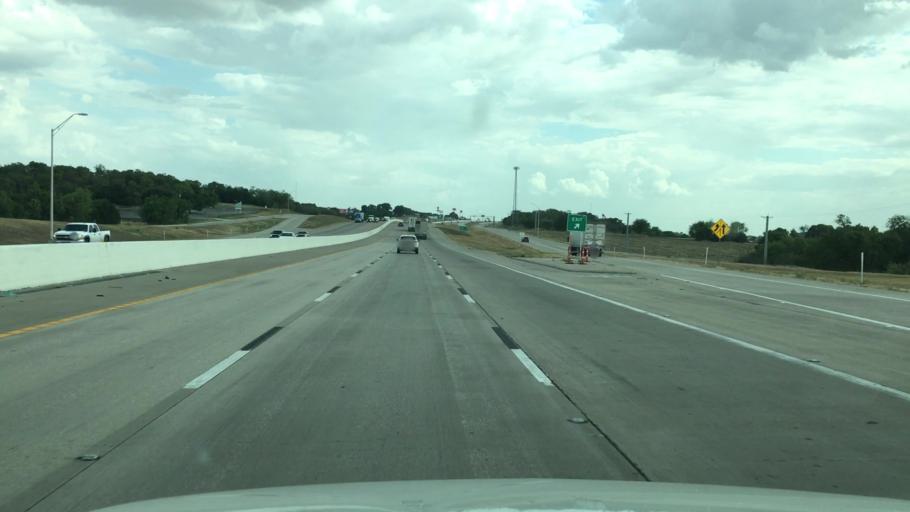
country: US
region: Texas
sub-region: McLennan County
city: West
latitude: 31.8167
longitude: -97.0984
